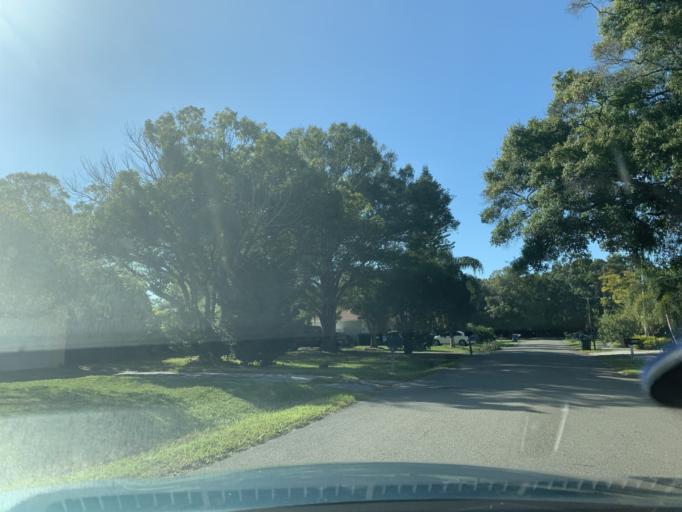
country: US
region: Florida
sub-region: Pinellas County
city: Belleair
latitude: 27.9251
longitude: -82.7993
